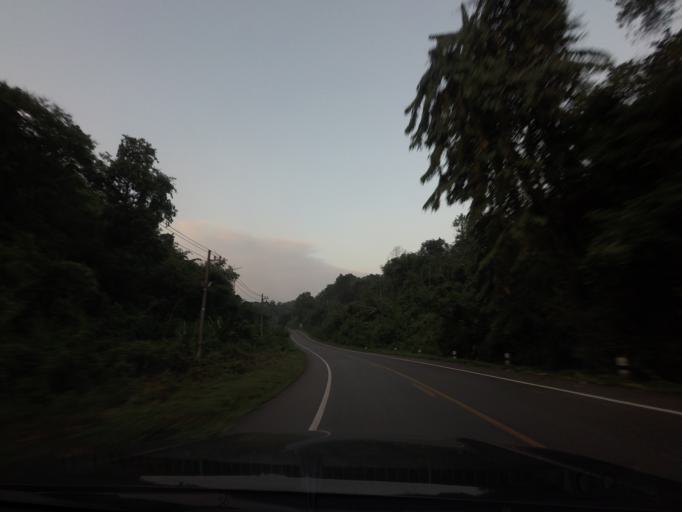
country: TH
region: Nan
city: Na Noi
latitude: 18.4327
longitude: 100.7057
